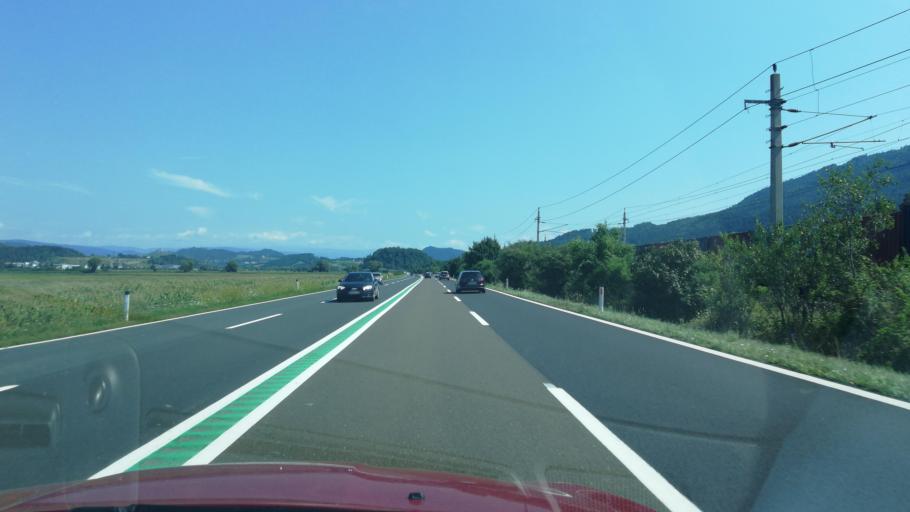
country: AT
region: Carinthia
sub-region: Politischer Bezirk Klagenfurt Land
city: Maria Saal
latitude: 46.7118
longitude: 14.3681
